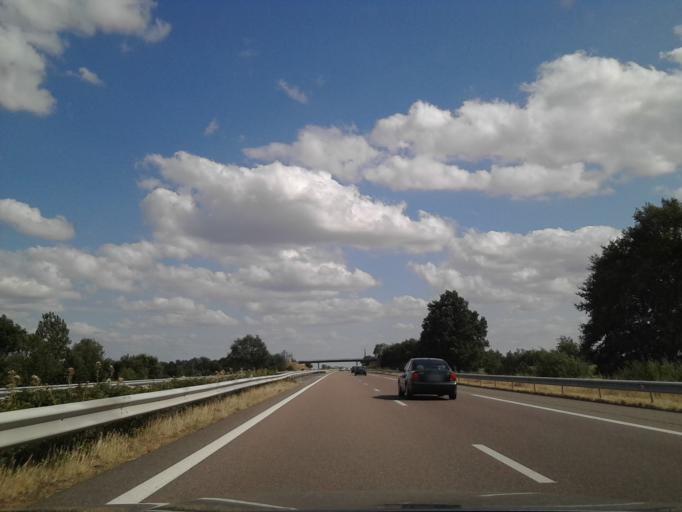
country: FR
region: Auvergne
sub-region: Departement de l'Allier
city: Estivareilles
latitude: 46.4623
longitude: 2.6819
